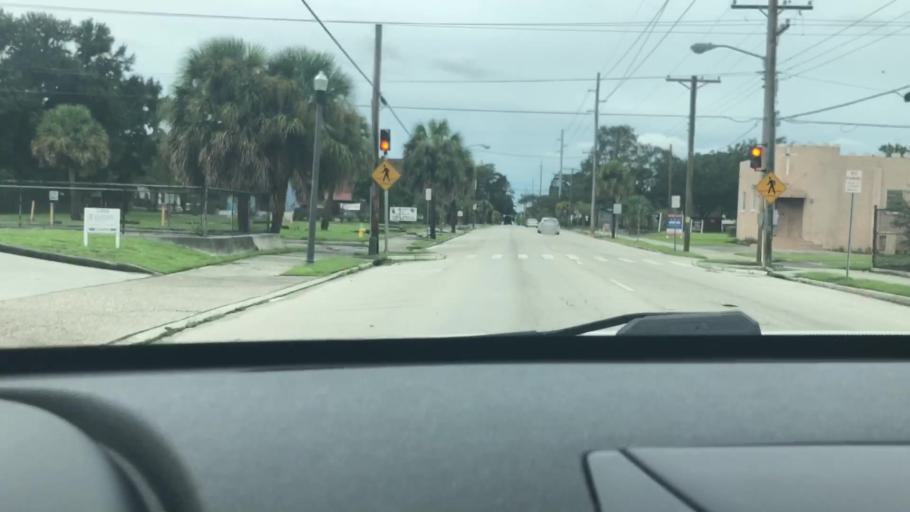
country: US
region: Florida
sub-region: Hillsborough County
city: Tampa
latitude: 27.9620
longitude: -82.4829
